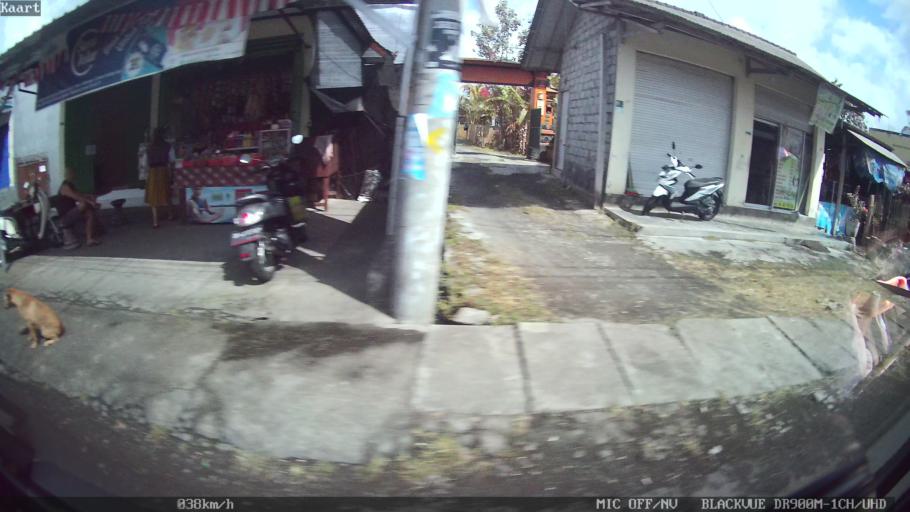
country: ID
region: Bali
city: Banjar Karangsuling
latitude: -8.5995
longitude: 115.2026
